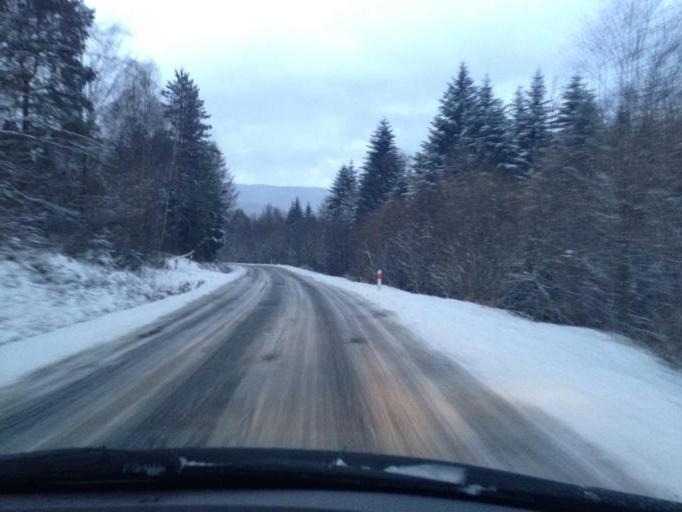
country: PL
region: Subcarpathian Voivodeship
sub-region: Powiat jasielski
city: Krempna
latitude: 49.5282
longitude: 21.5015
